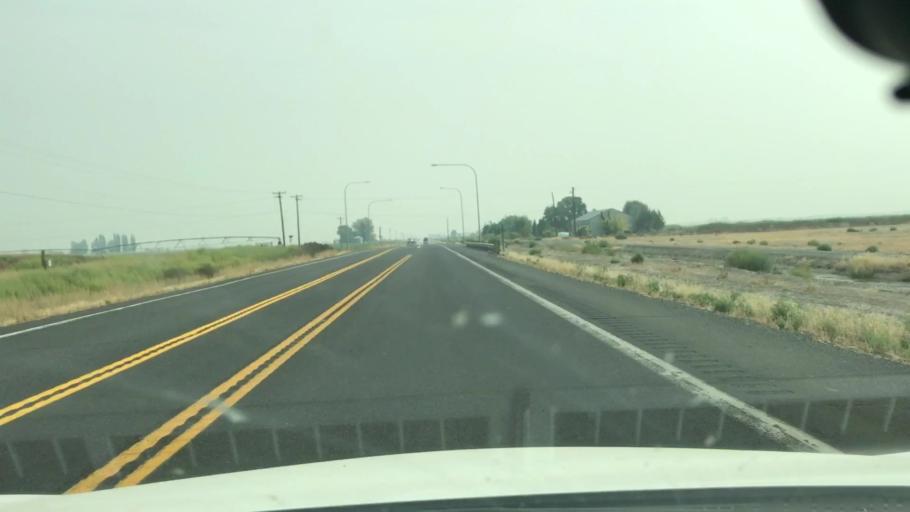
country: US
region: Washington
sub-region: Grant County
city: Quincy
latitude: 47.2341
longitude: -119.8128
